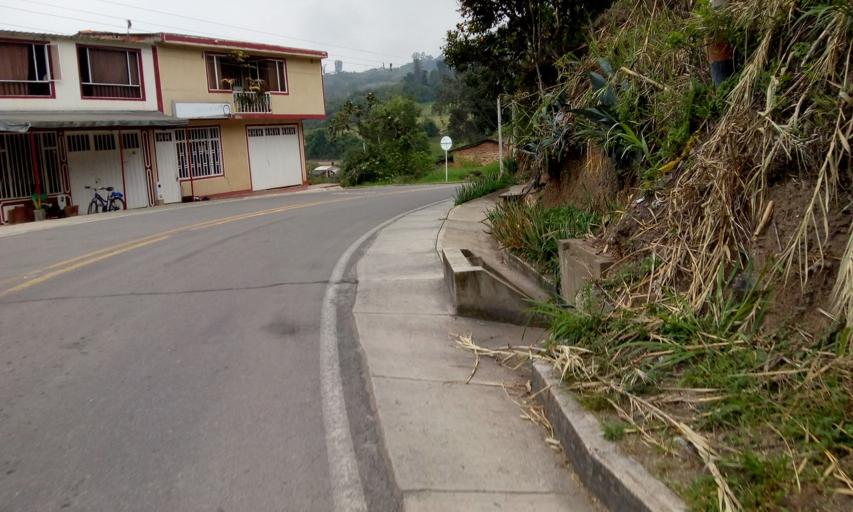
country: CO
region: Boyaca
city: Tipacoque
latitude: 6.4168
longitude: -72.6920
